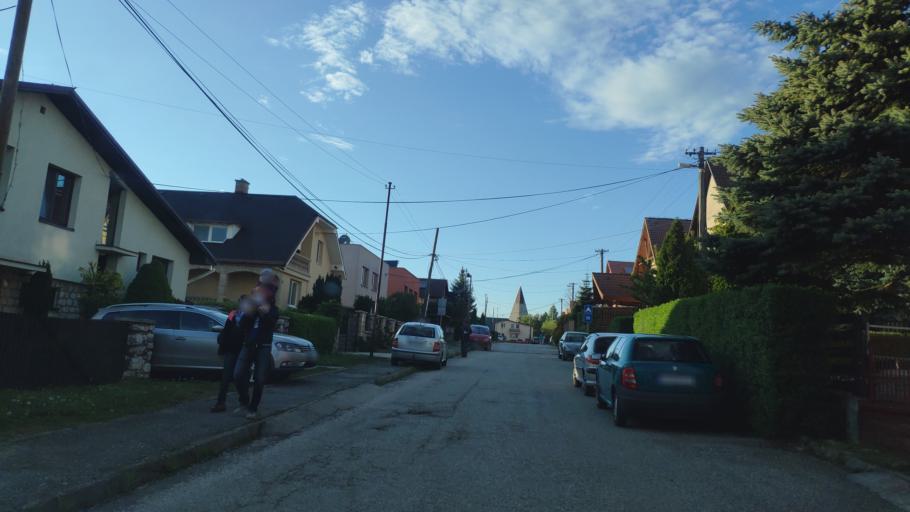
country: SK
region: Kosicky
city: Kosice
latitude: 48.7505
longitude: 21.3472
